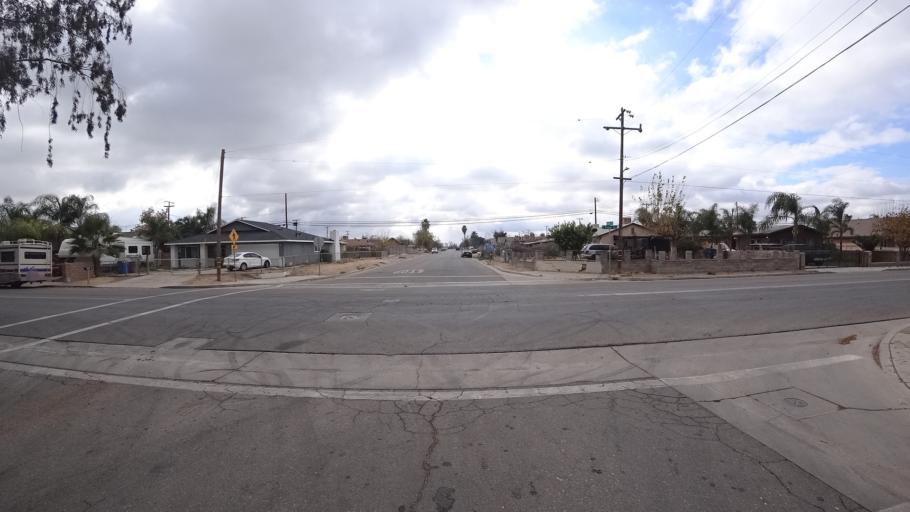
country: US
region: California
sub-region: Kern County
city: Bakersfield
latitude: 35.3251
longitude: -118.9899
